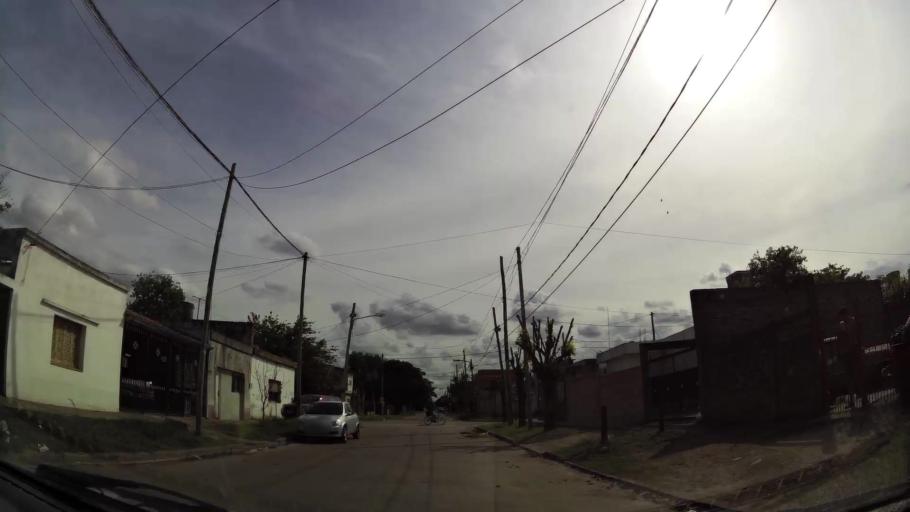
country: AR
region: Buenos Aires
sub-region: Partido de Quilmes
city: Quilmes
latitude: -34.7707
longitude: -58.2522
